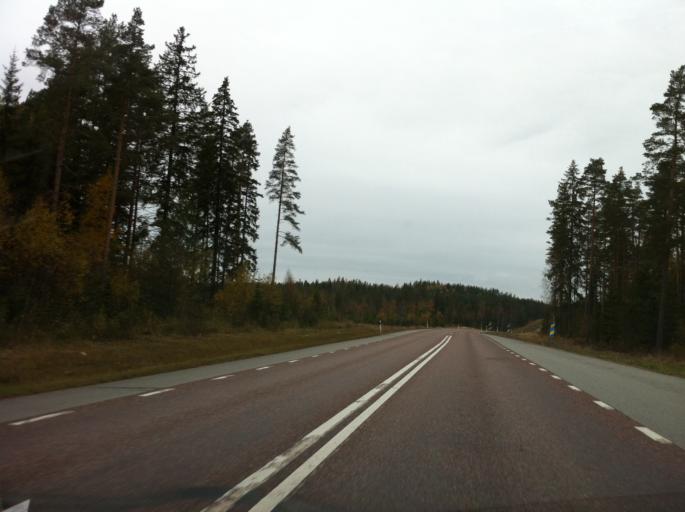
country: SE
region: Dalarna
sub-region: Ludvika Kommun
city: Grangesberg
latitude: 59.9980
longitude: 15.0104
